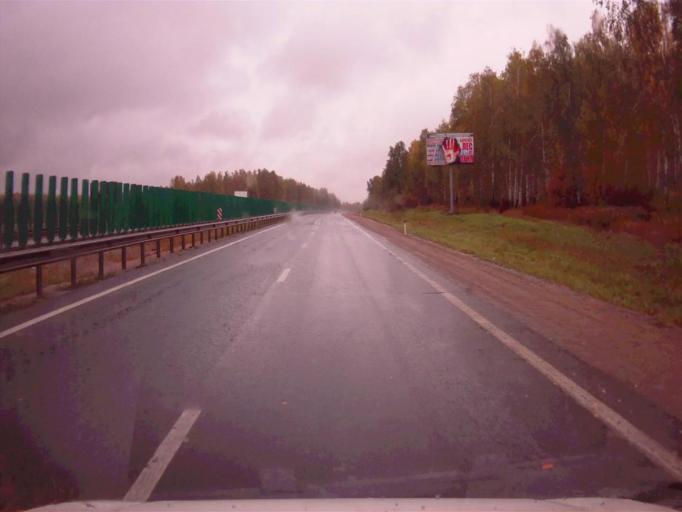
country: RU
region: Chelyabinsk
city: Dolgoderevenskoye
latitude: 55.3319
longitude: 61.3179
